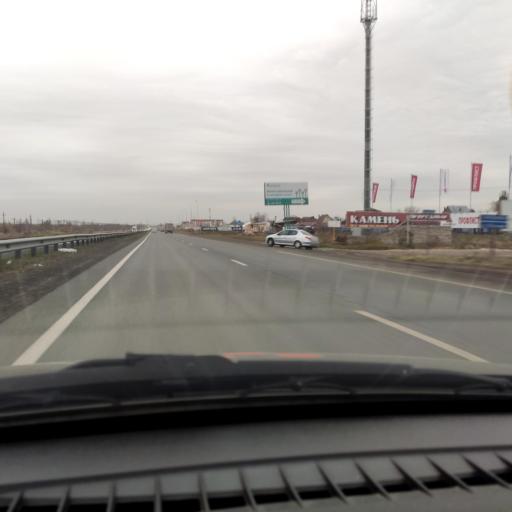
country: RU
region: Samara
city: Tol'yatti
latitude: 53.5681
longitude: 49.3772
